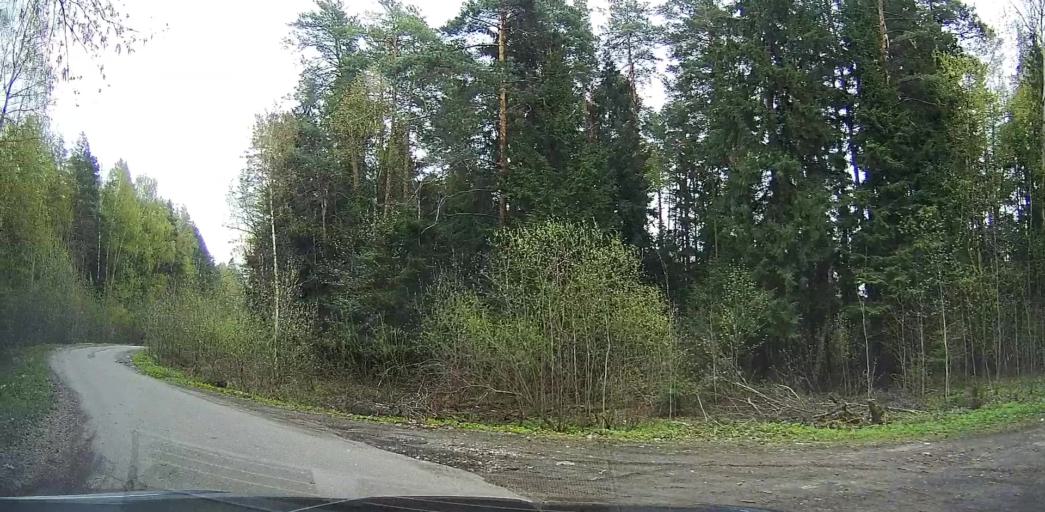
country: RU
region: Moskovskaya
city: Malyshevo
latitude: 55.5544
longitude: 38.3383
